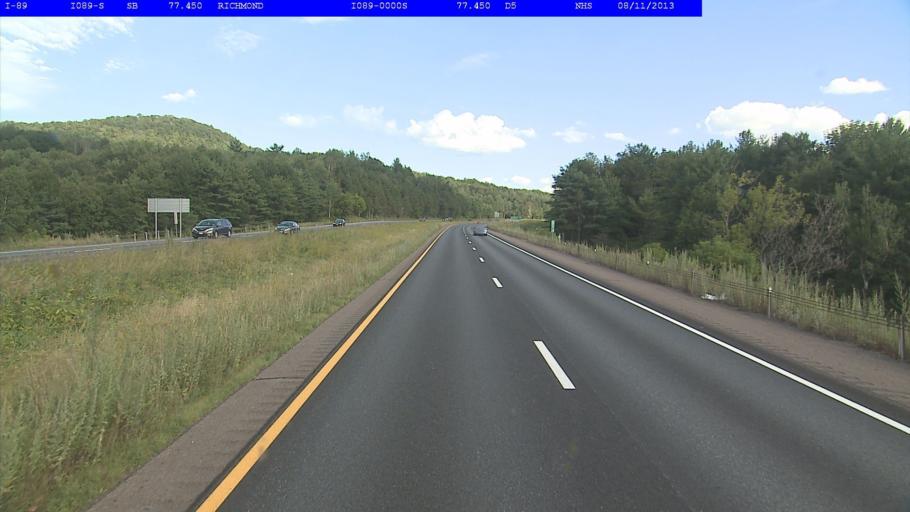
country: US
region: Vermont
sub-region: Chittenden County
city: Williston
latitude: 44.4159
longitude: -72.9953
